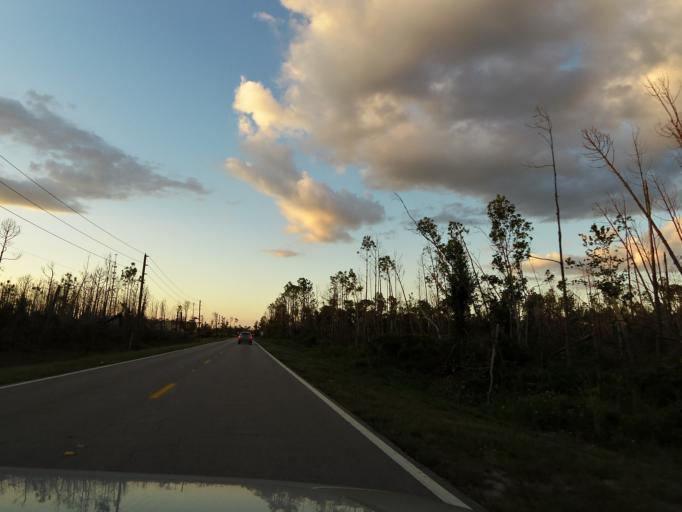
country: US
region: Florida
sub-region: Bay County
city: Mexico Beach
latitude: 29.9377
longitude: -85.3886
